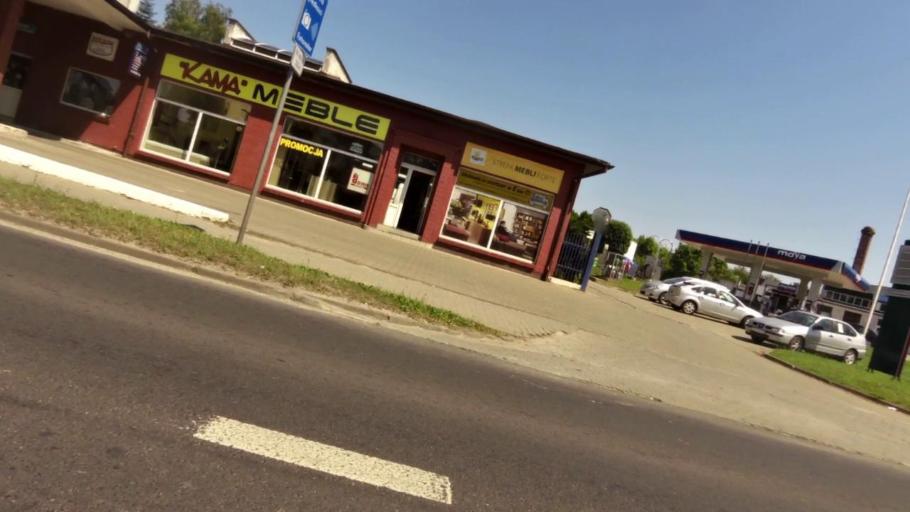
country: PL
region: West Pomeranian Voivodeship
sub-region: Powiat swidwinski
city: Polczyn-Zdroj
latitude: 53.7701
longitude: 16.0910
